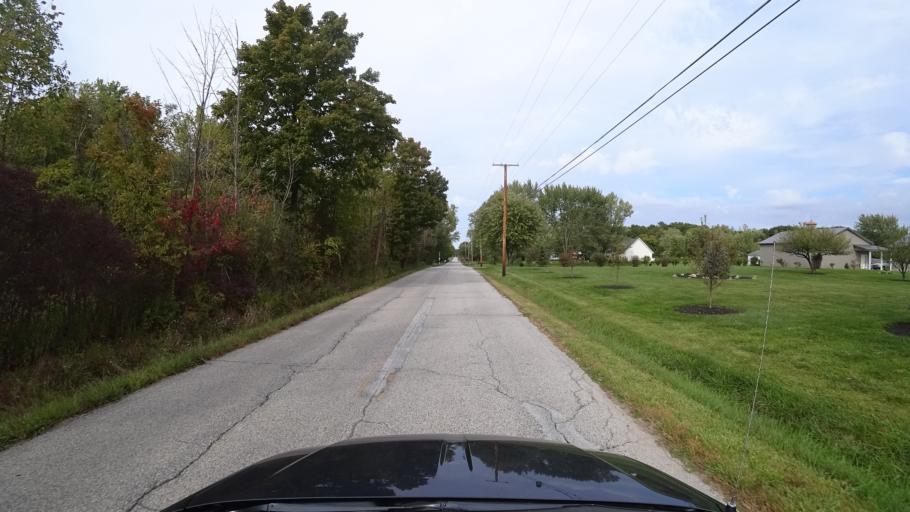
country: US
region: Indiana
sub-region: LaPorte County
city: Trail Creek
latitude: 41.7008
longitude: -86.8163
